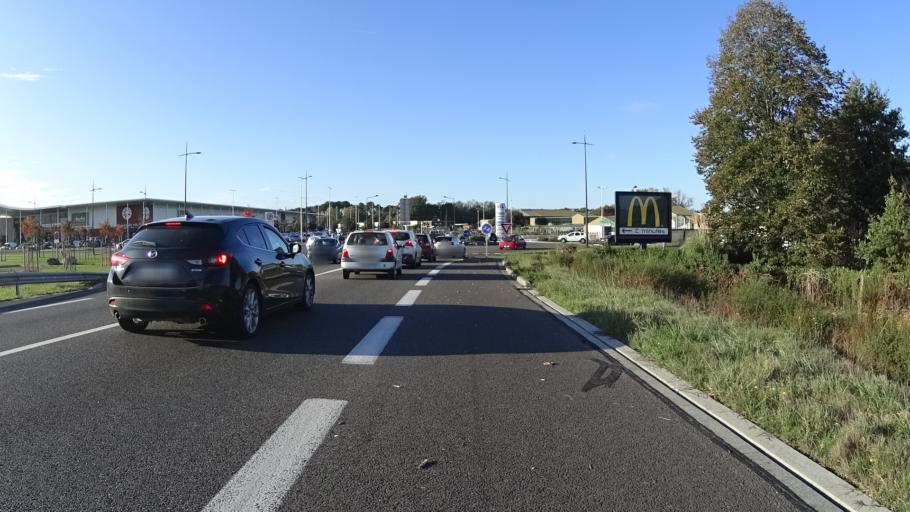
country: FR
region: Aquitaine
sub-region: Departement des Landes
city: Saint-Paul-les-Dax
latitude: 43.7293
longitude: -1.0375
